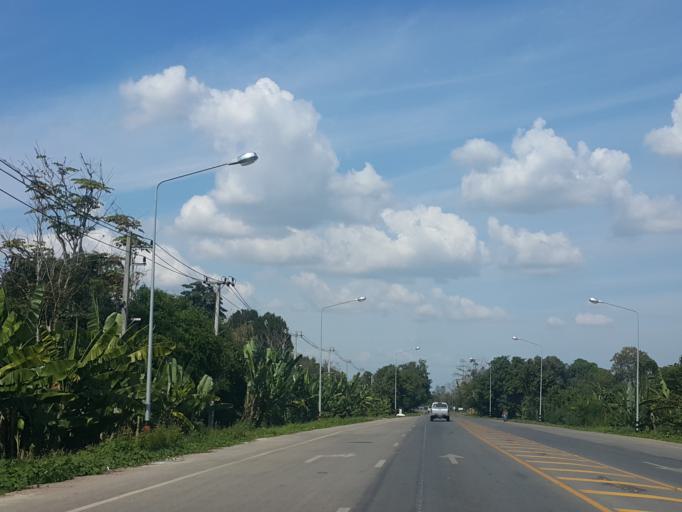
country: TH
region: Sukhothai
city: Si Samrong
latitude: 17.2397
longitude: 99.8465
